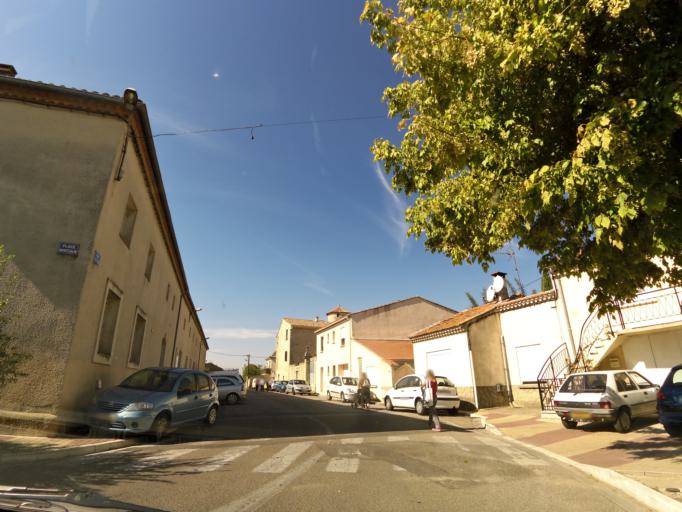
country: FR
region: Languedoc-Roussillon
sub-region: Departement du Gard
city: Vestric-et-Candiac
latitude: 43.7409
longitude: 4.2596
